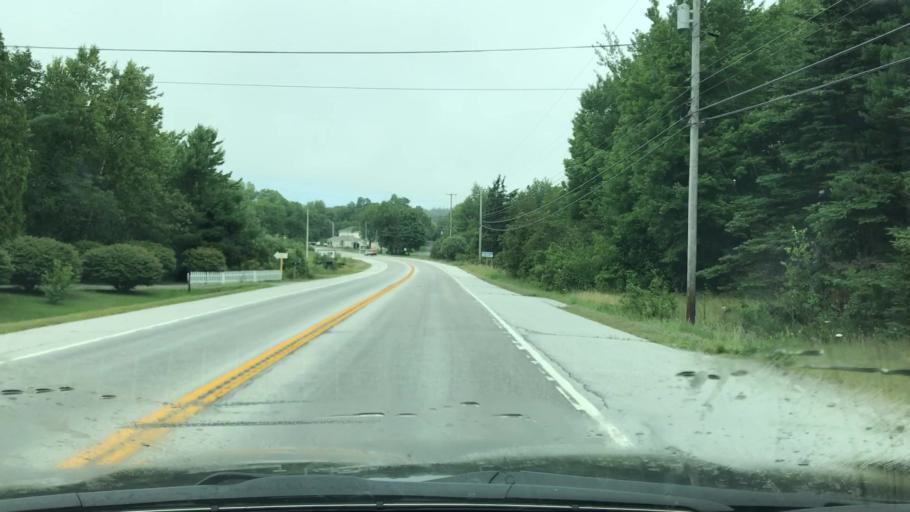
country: US
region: Maine
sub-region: Waldo County
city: Northport
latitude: 44.3312
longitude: -68.9574
